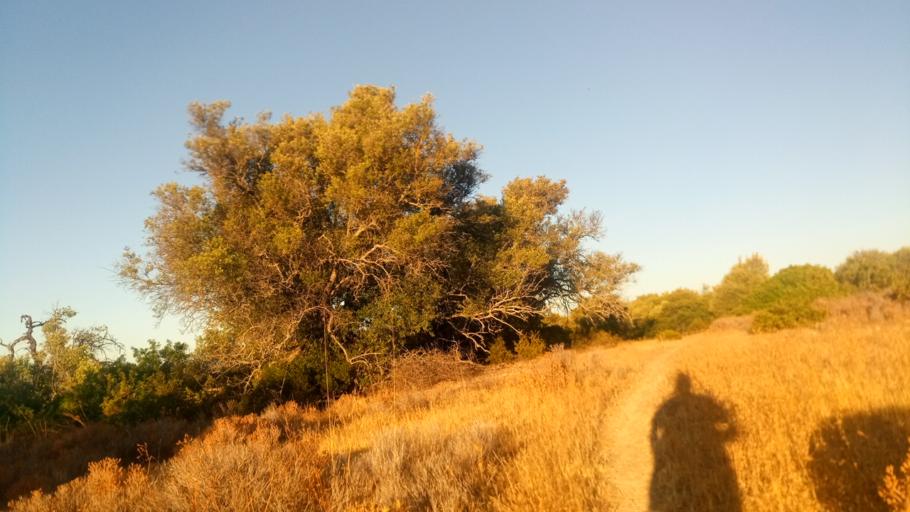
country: PT
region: Faro
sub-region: Tavira
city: Tavira
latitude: 37.1414
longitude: -7.6117
